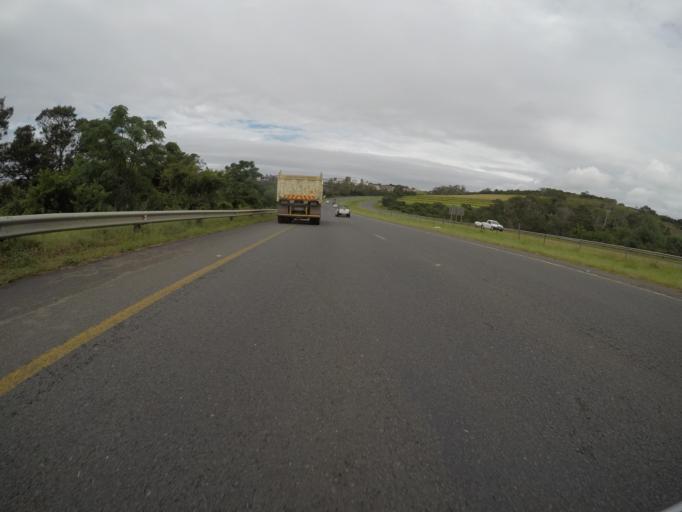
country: ZA
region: Eastern Cape
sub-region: Buffalo City Metropolitan Municipality
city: East London
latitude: -32.9443
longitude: 27.9422
